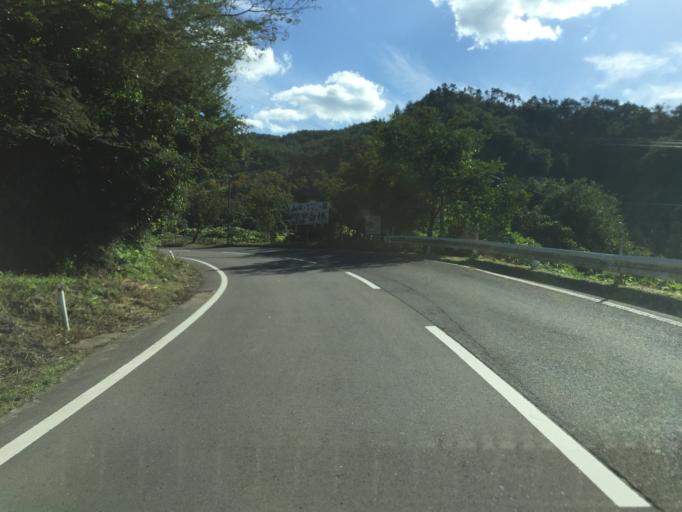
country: JP
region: Fukushima
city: Yanagawamachi-saiwaicho
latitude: 37.8534
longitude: 140.6454
